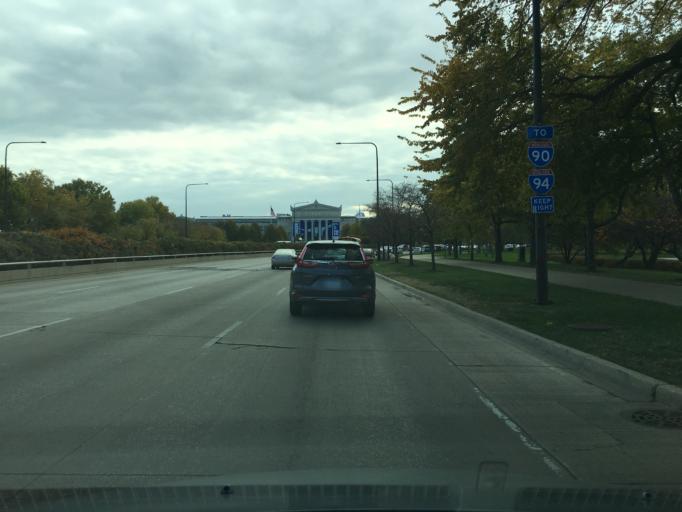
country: US
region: Illinois
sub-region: Cook County
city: Chicago
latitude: 41.8706
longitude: -87.6173
